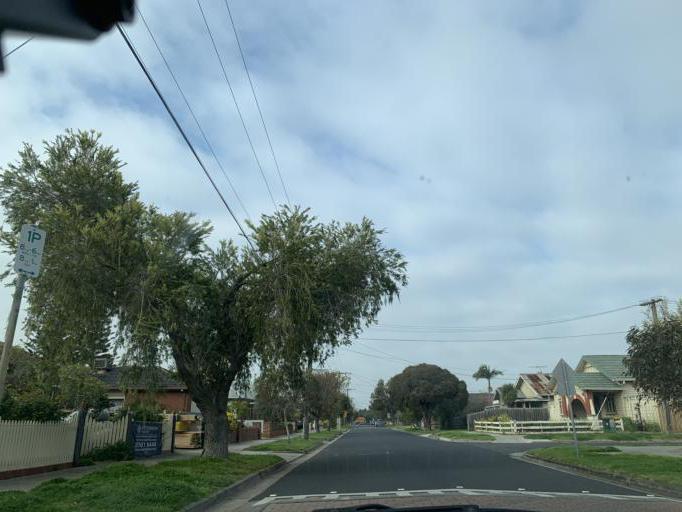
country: AU
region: Victoria
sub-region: Moreland
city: Pascoe Vale South
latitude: -37.7365
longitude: 144.9446
